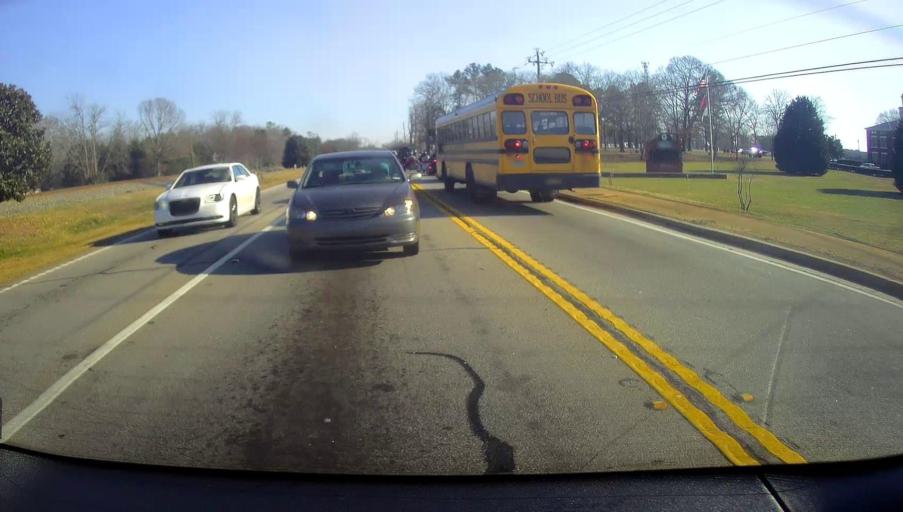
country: US
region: Georgia
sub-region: Henry County
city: Locust Grove
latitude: 33.3533
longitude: -84.1135
